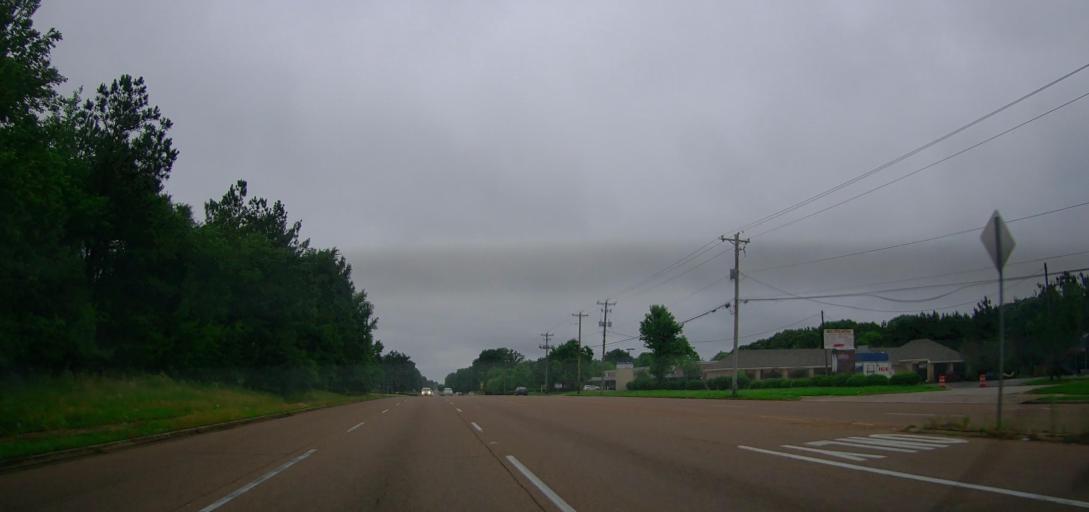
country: US
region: Mississippi
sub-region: De Soto County
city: Olive Branch
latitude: 35.0065
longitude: -89.8311
